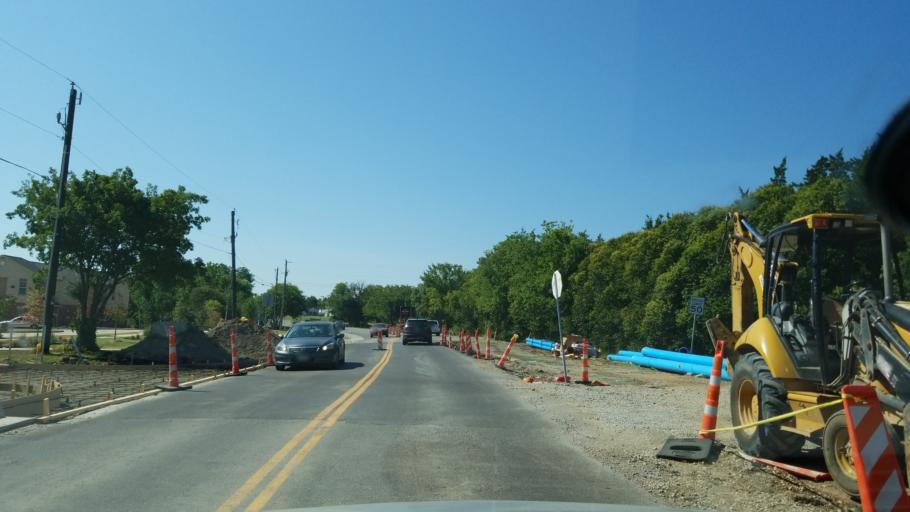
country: US
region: Texas
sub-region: Tarrant County
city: Mansfield
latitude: 32.5589
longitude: -97.1422
